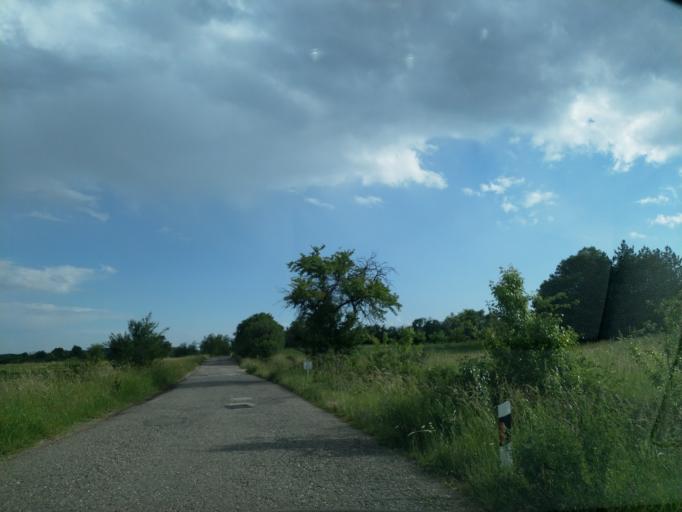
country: RS
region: Central Serbia
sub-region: Borski Okrug
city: Bor
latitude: 43.9841
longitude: 21.9736
